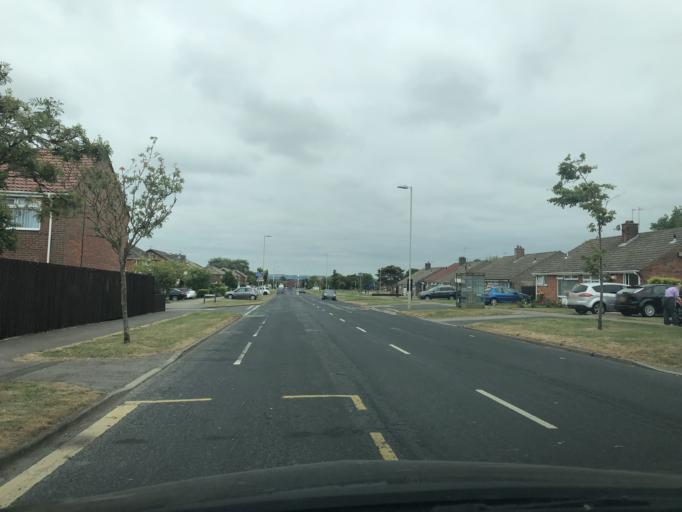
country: GB
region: England
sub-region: North Yorkshire
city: Scarborough
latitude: 54.2433
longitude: -0.3892
